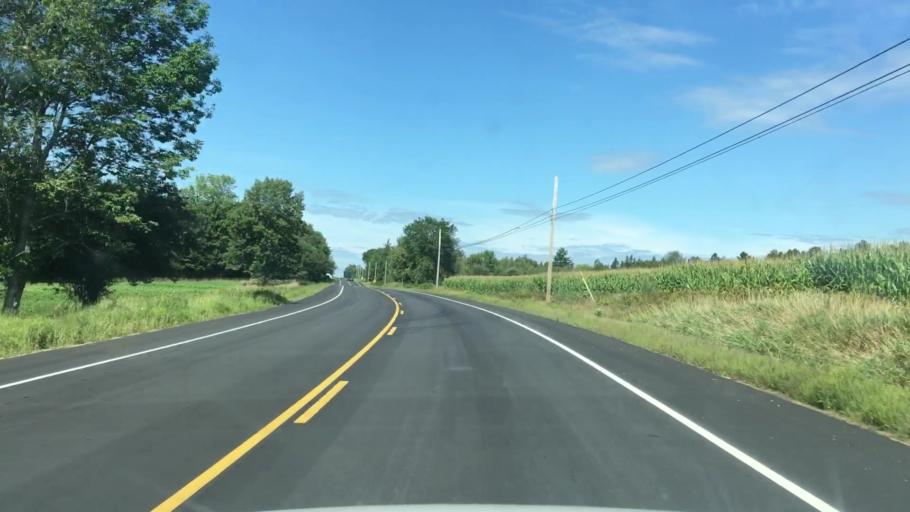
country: US
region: Maine
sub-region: Penobscot County
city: Corinna
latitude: 44.9496
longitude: -69.2485
